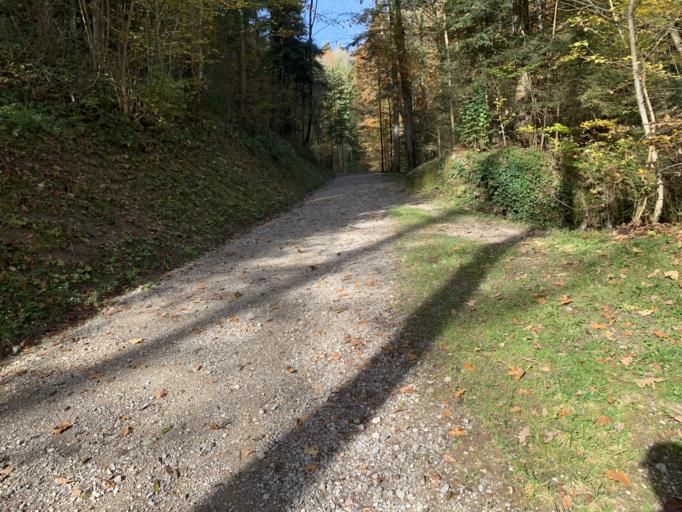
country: CH
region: Zurich
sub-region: Bezirk Hinwil
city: Hinwil
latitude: 47.3072
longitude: 8.8545
